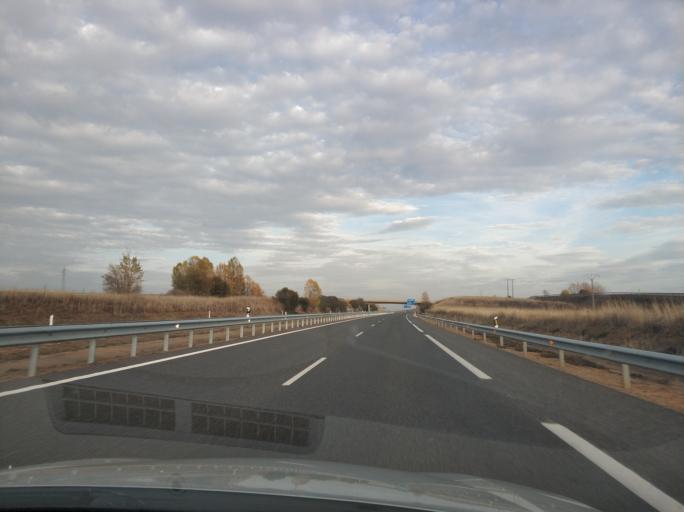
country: ES
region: Castille and Leon
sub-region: Provincia de Palencia
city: Abia de las Torres
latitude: 42.3990
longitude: -4.4143
